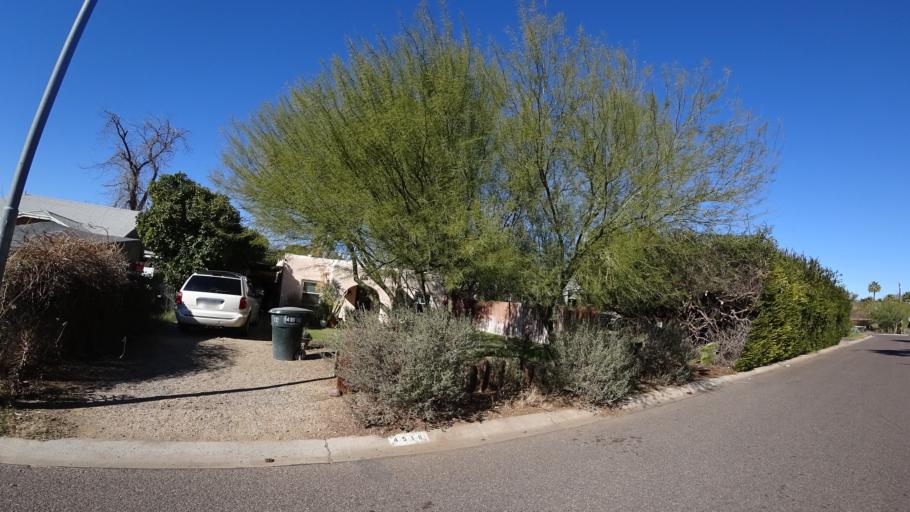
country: US
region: Arizona
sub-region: Maricopa County
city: Phoenix
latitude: 33.5030
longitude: -112.0531
